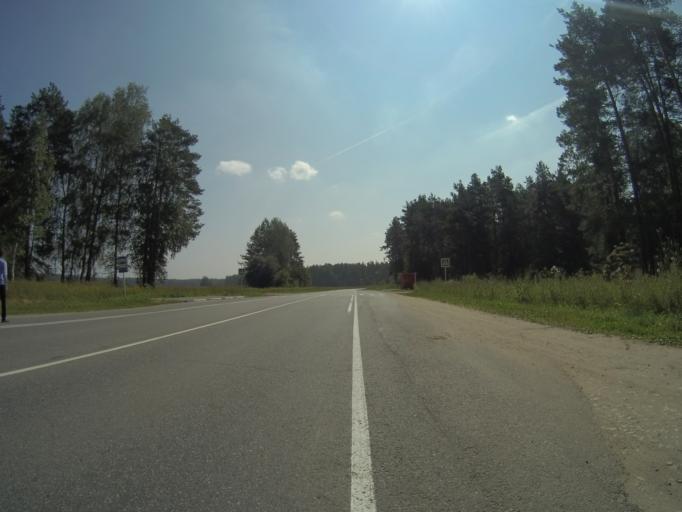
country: RU
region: Vladimir
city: Anopino
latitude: 55.7051
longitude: 40.7392
